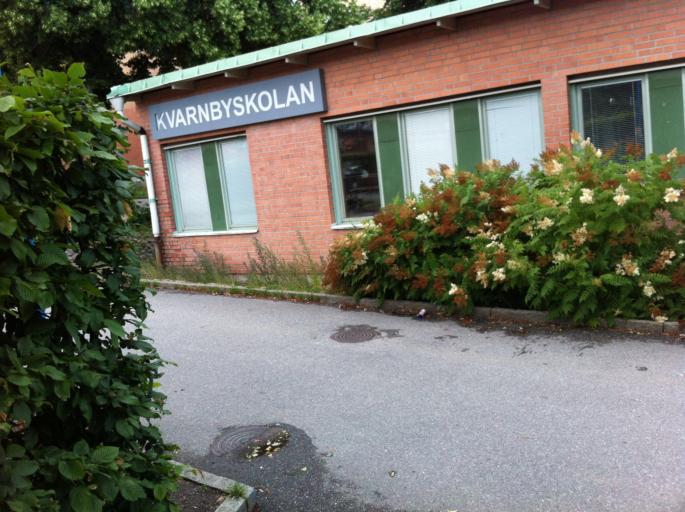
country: SE
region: Stockholm
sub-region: Stockholms Kommun
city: Kista
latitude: 59.3874
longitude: 17.9294
